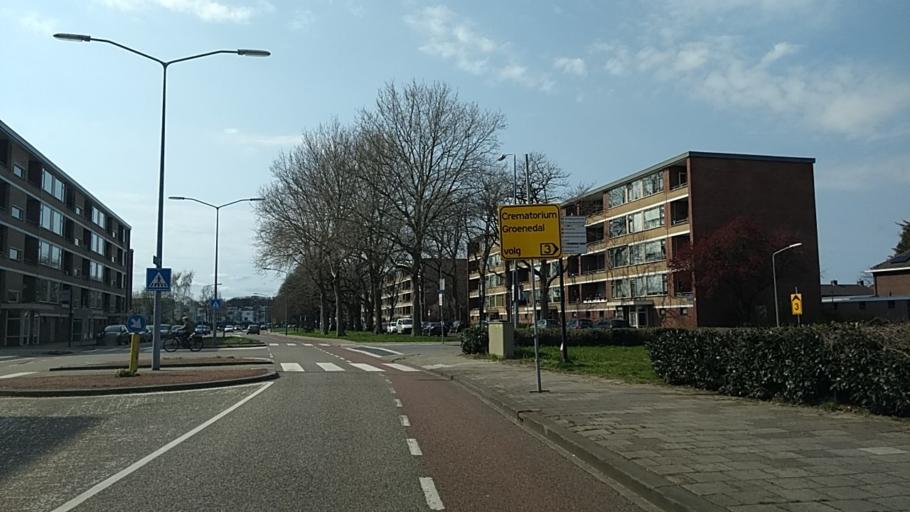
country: NL
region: Overijssel
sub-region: Gemeente Almelo
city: Almelo
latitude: 52.3447
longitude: 6.6486
